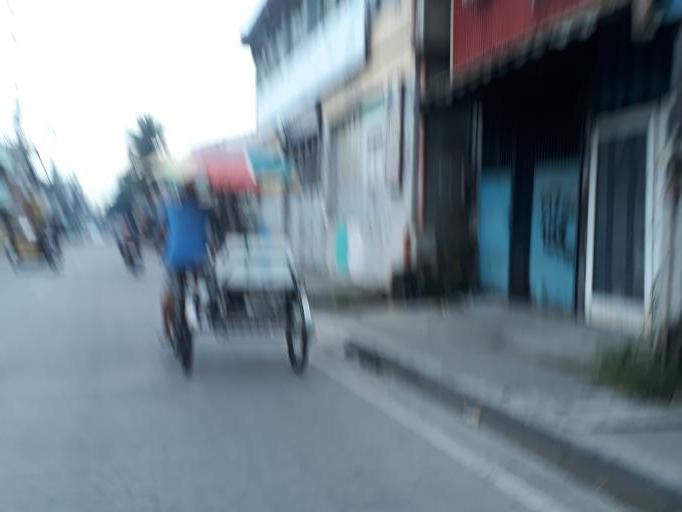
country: PH
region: Calabarzon
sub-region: Province of Rizal
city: Valenzuela
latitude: 14.6968
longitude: 120.9532
